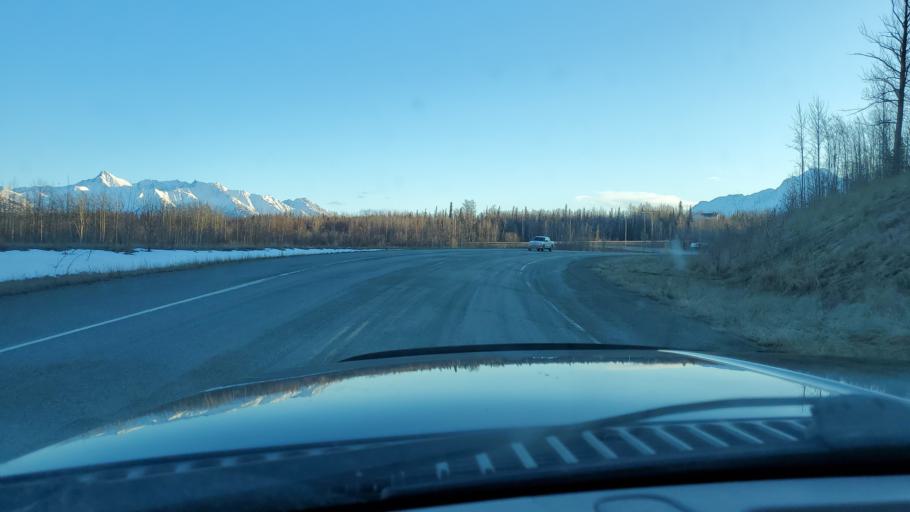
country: US
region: Alaska
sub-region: Matanuska-Susitna Borough
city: Gateway
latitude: 61.5940
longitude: -149.2439
